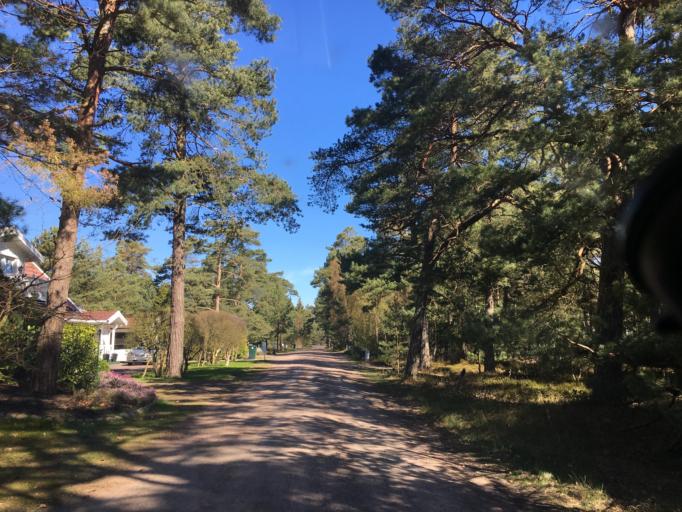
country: SE
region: Skane
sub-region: Vellinge Kommun
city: Ljunghusen
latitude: 55.3974
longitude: 12.9281
